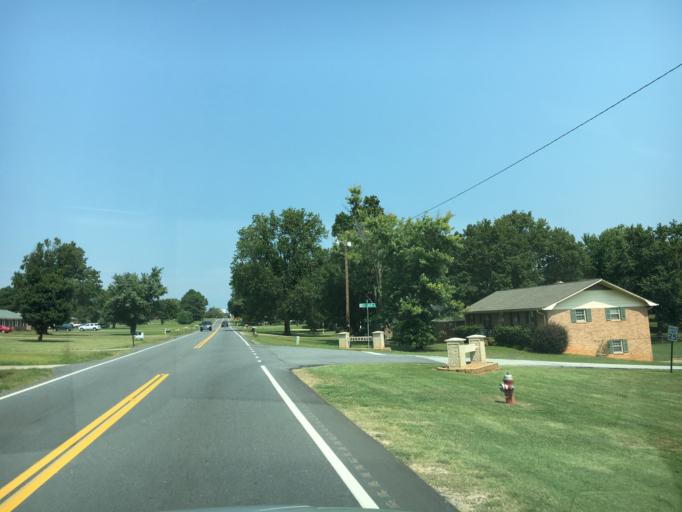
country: US
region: South Carolina
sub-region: Spartanburg County
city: Valley Falls
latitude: 35.0178
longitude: -81.9490
